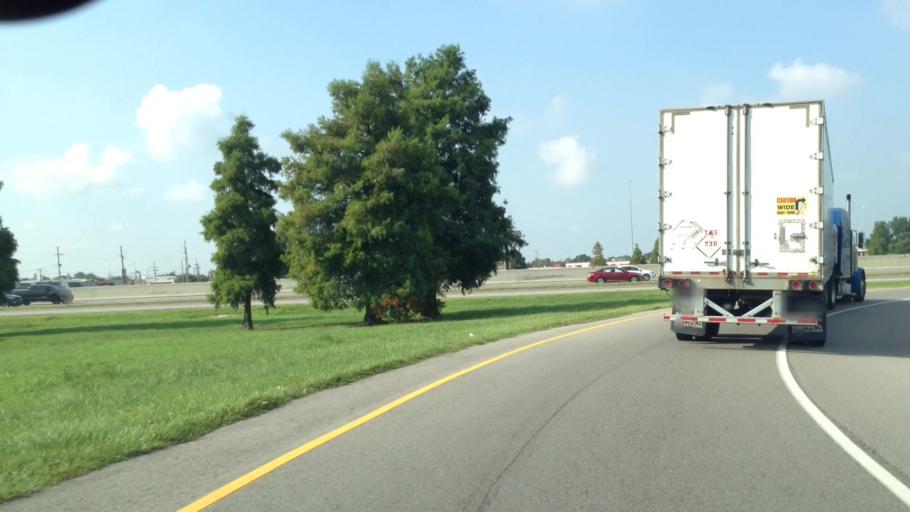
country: US
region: Louisiana
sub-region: Jefferson Parish
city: Metairie Terrace
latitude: 29.9998
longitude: -90.1826
